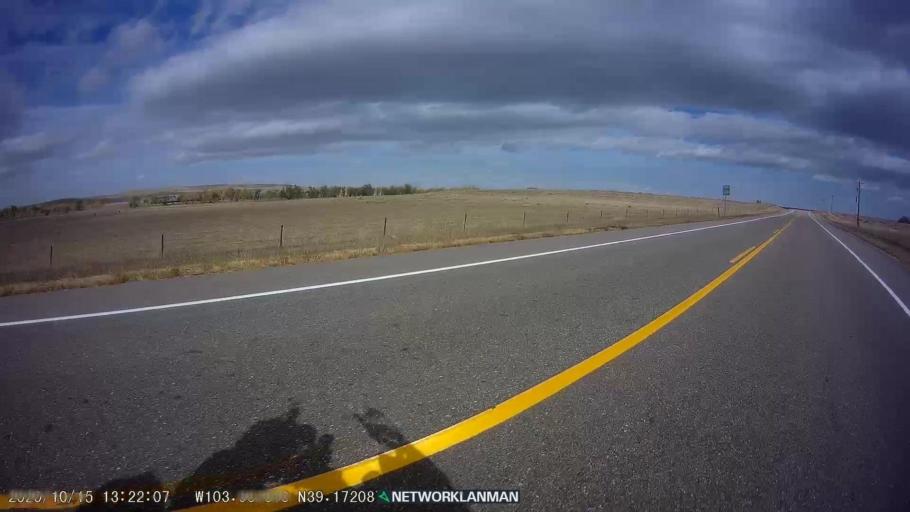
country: US
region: Colorado
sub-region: Lincoln County
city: Limon
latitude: 39.1722
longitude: -103.9620
